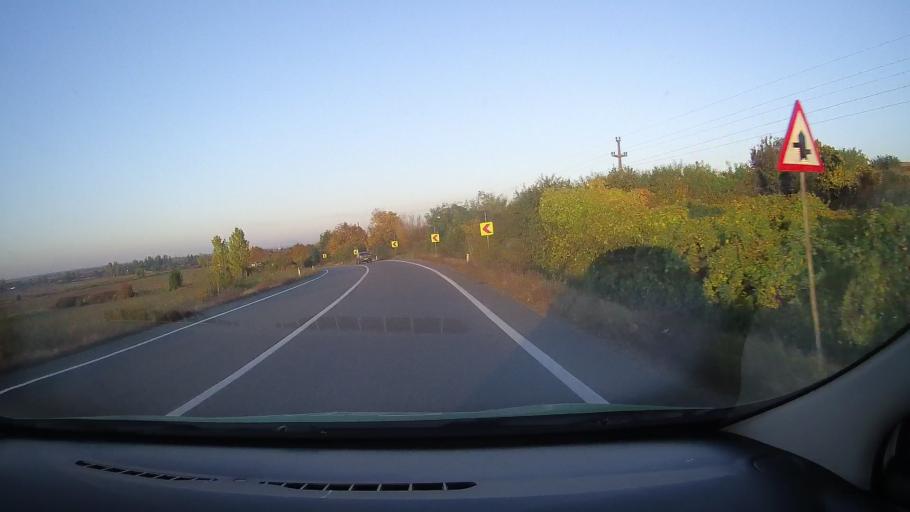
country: RO
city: Dioszeg
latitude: 47.2774
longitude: 21.9827
